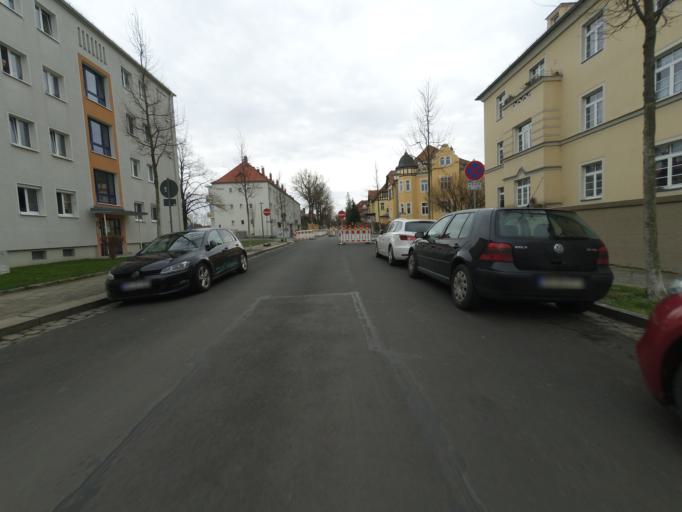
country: DE
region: Saxony
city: Heidenau
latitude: 51.0077
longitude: 13.8247
